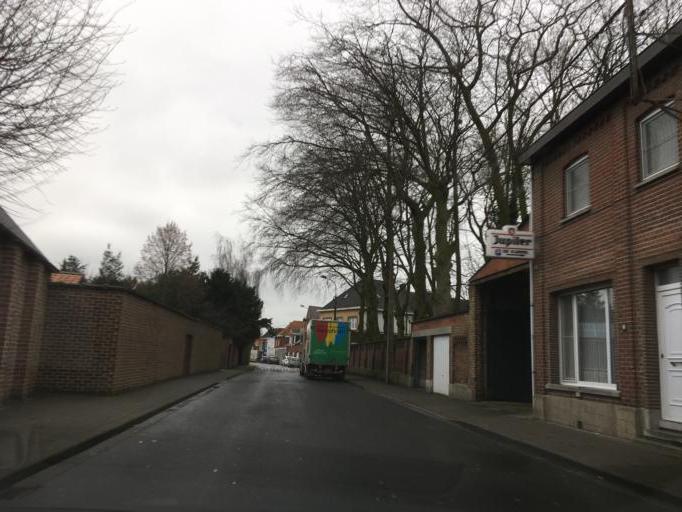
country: BE
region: Flanders
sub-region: Provincie West-Vlaanderen
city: Roeselare
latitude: 50.9693
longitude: 3.1411
